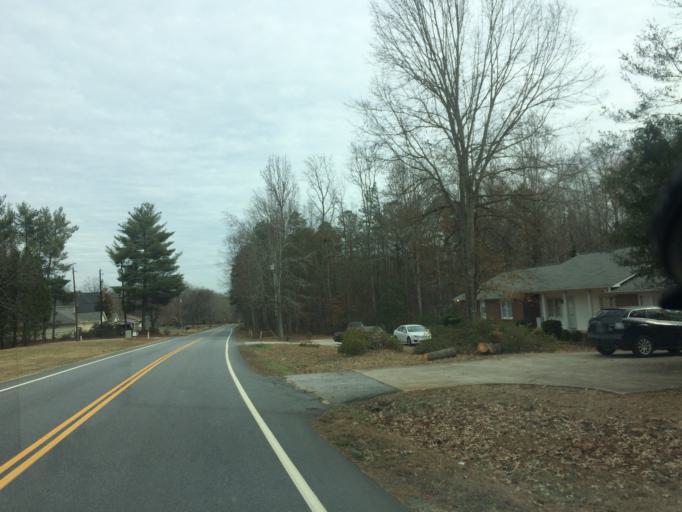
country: US
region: South Carolina
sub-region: Spartanburg County
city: Duncan
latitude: 34.8807
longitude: -82.1067
